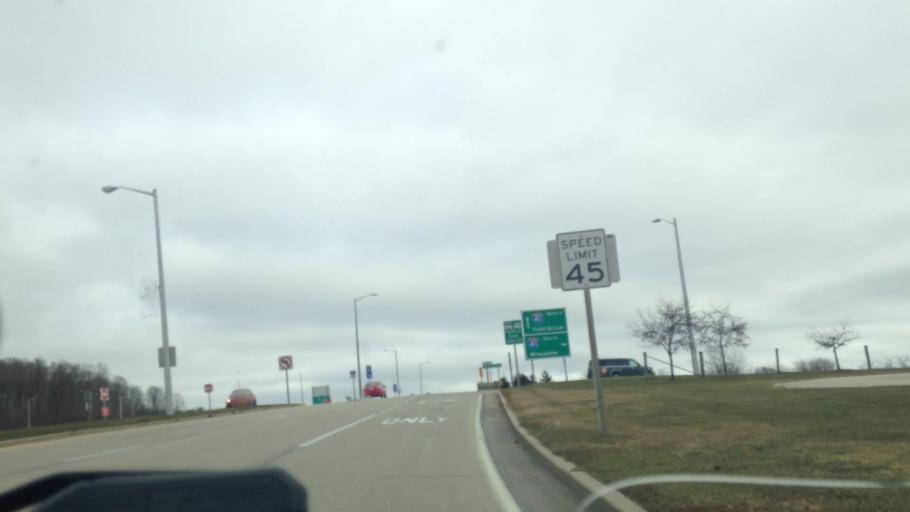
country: US
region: Wisconsin
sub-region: Washington County
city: Slinger
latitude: 43.4234
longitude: -88.3377
